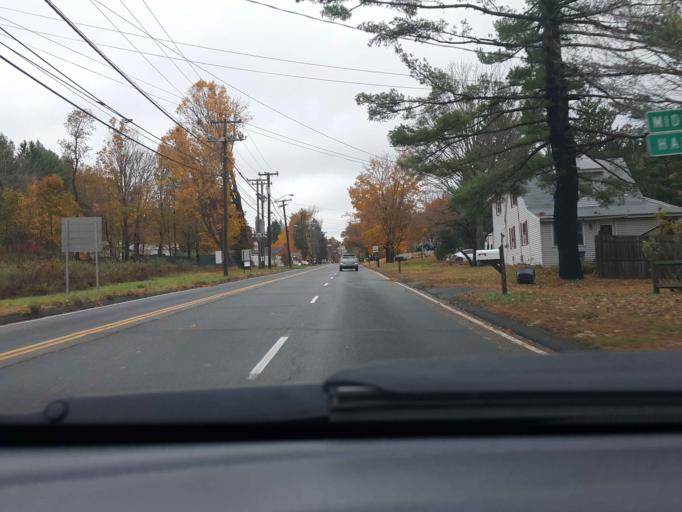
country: US
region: Connecticut
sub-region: Middlesex County
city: Durham
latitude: 41.4871
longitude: -72.6816
